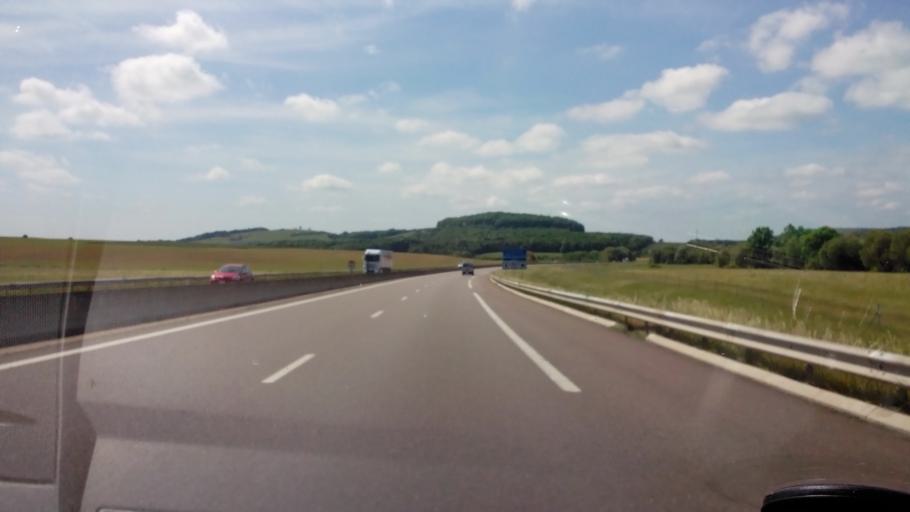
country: FR
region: Lorraine
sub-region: Departement des Vosges
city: Chatenois
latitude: 48.3608
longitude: 5.8661
